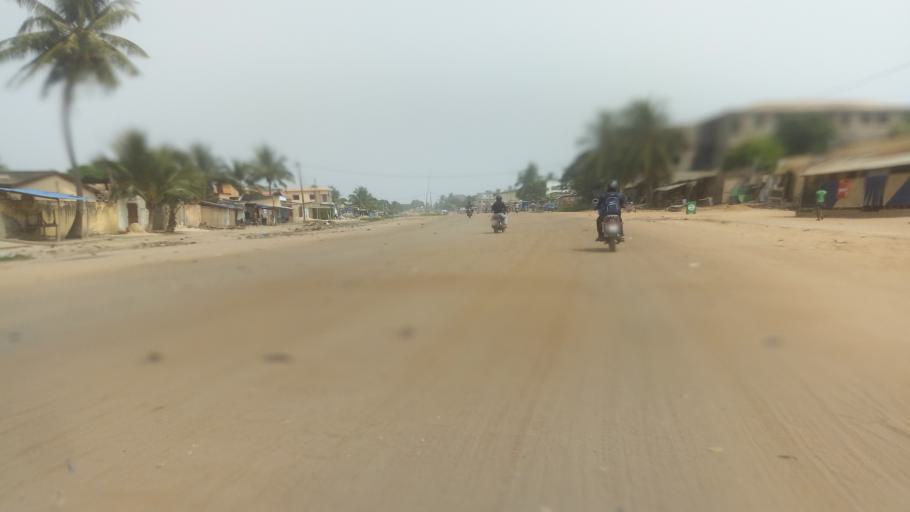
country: TG
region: Maritime
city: Lome
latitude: 6.1857
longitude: 1.1736
